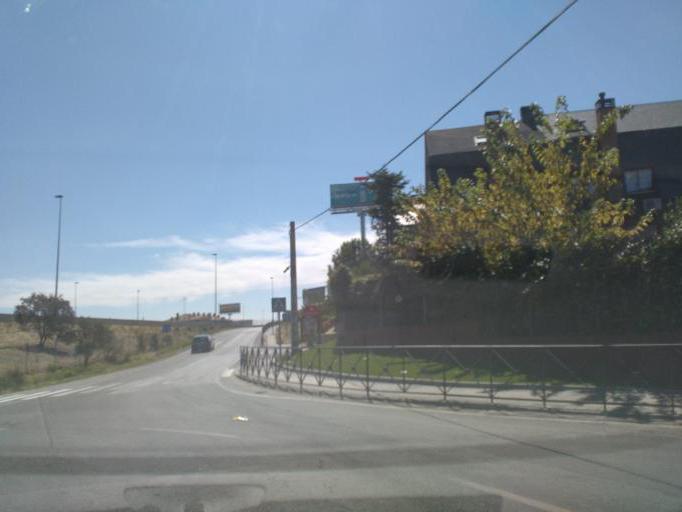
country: ES
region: Madrid
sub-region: Provincia de Madrid
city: Las Matas
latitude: 40.5573
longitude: -3.9012
